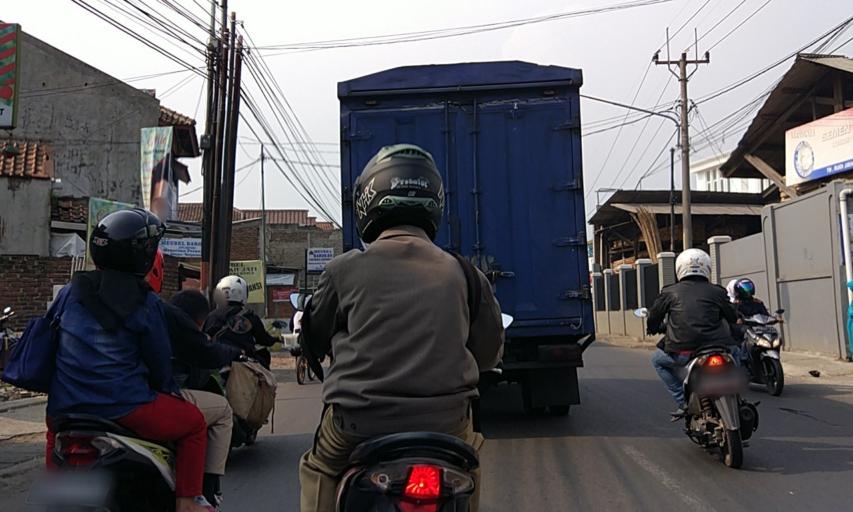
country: ID
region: West Java
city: Margahayukencana
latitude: -6.9860
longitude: 107.5604
